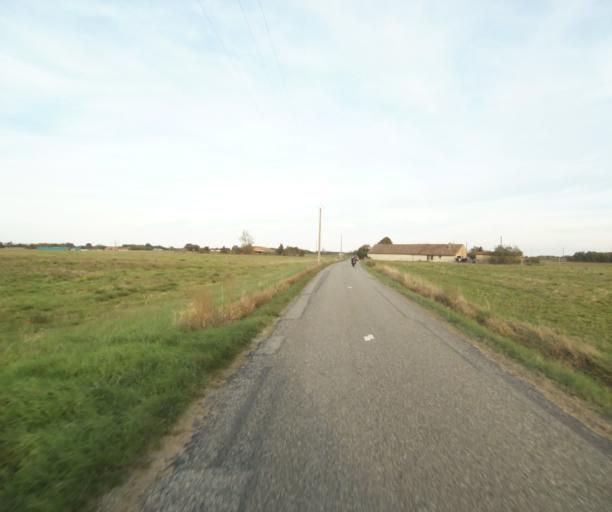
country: FR
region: Midi-Pyrenees
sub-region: Departement du Tarn-et-Garonne
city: Campsas
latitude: 43.8605
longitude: 1.3230
